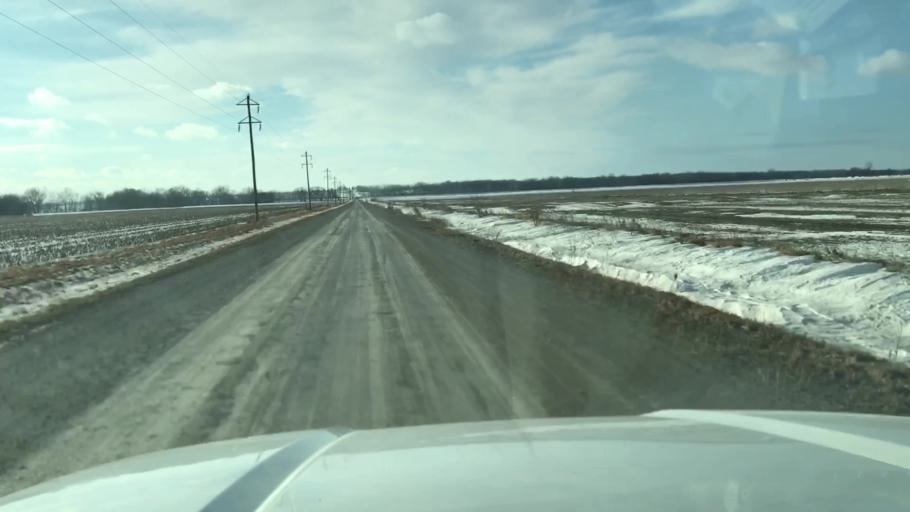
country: US
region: Missouri
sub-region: Holt County
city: Oregon
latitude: 40.1300
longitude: -95.0285
